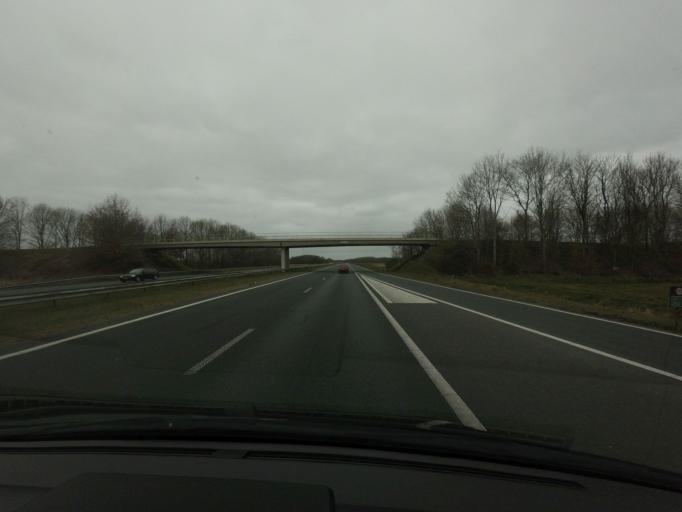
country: NL
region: Groningen
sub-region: Gemeente Hoogezand-Sappemeer
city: Hoogezand
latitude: 53.1892
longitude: 6.7119
